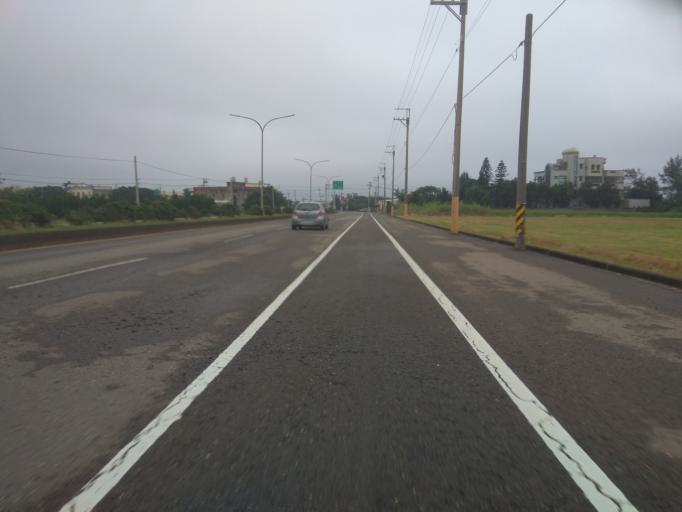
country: TW
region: Taiwan
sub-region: Hsinchu
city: Zhubei
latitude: 25.0302
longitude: 121.0768
